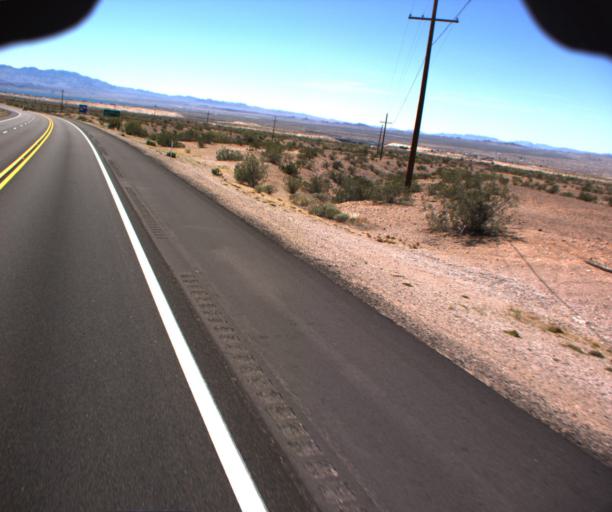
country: US
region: Arizona
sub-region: Mohave County
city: Desert Hills
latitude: 34.5937
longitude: -114.3695
